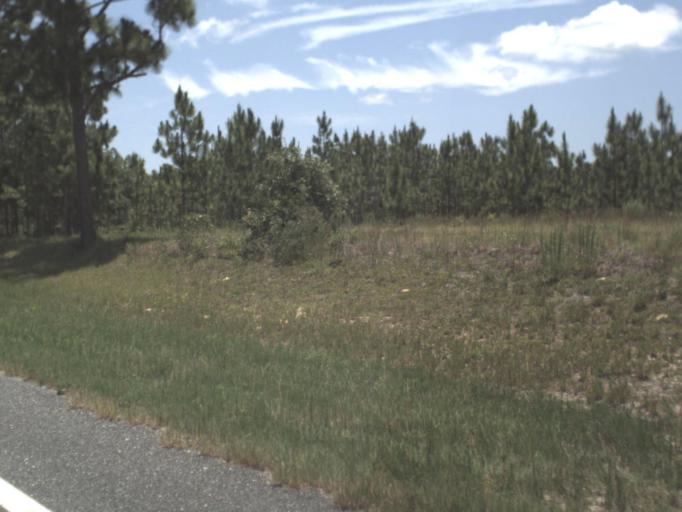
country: US
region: Florida
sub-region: Levy County
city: Williston Highlands
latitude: 29.2231
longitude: -82.5651
